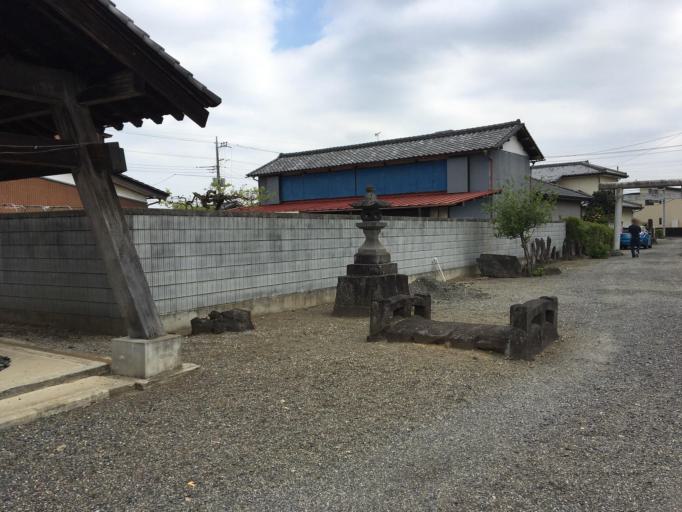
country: JP
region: Gunma
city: Isesaki
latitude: 36.2919
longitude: 139.1671
